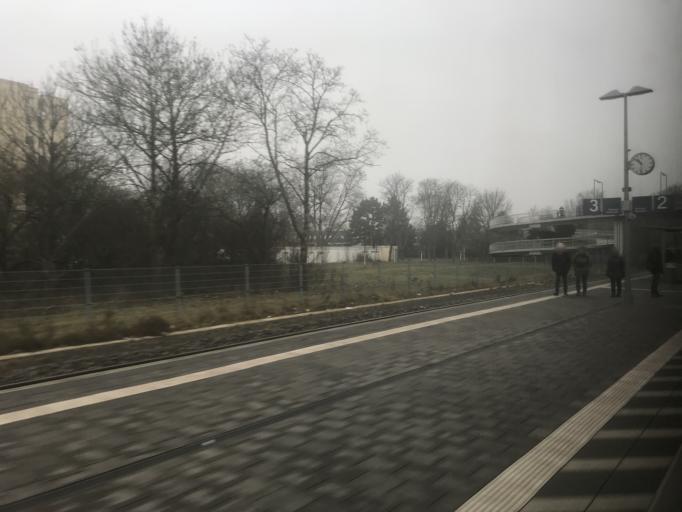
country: DE
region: Rheinland-Pfalz
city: Frankenthal
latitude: 49.5221
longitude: 8.3495
